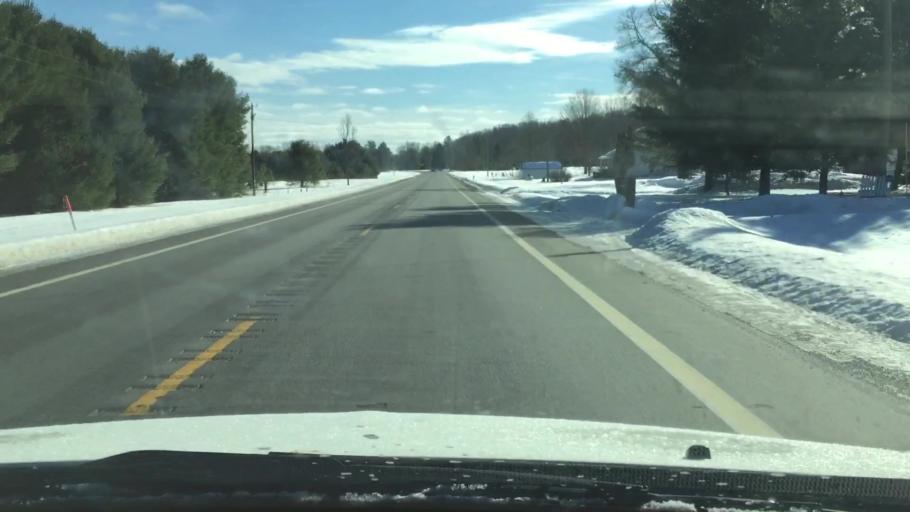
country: US
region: Michigan
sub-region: Charlevoix County
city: East Jordan
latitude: 45.0720
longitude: -85.0860
